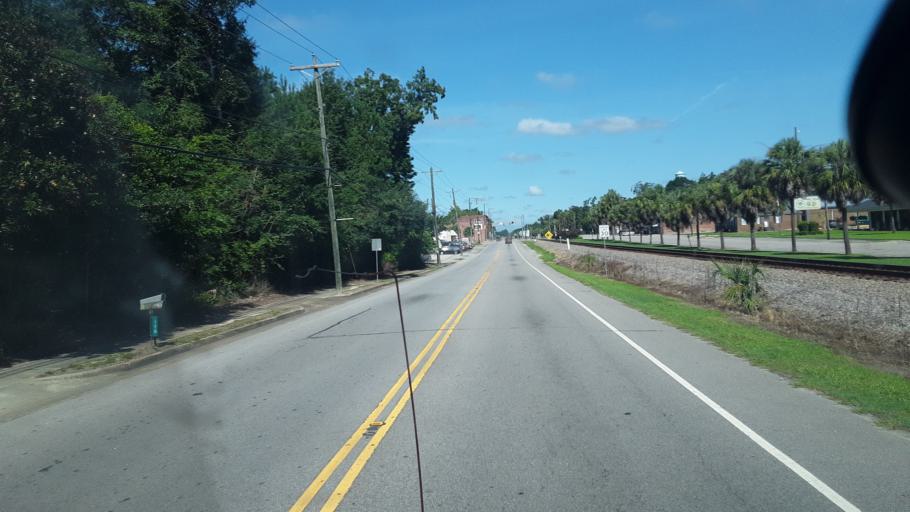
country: US
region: South Carolina
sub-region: Hampton County
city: Varnville
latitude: 32.8487
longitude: -81.0781
